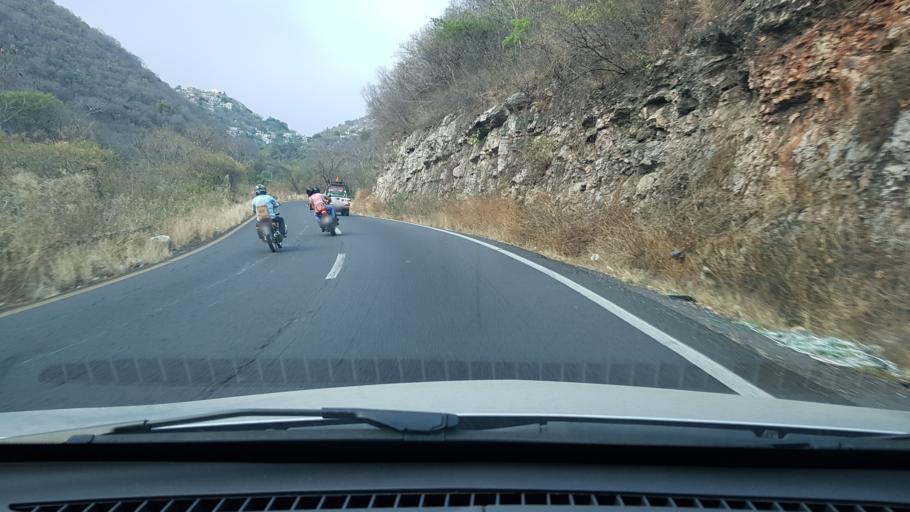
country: MX
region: Morelos
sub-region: Jiutepec
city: Independencia
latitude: 18.8681
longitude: -99.1196
